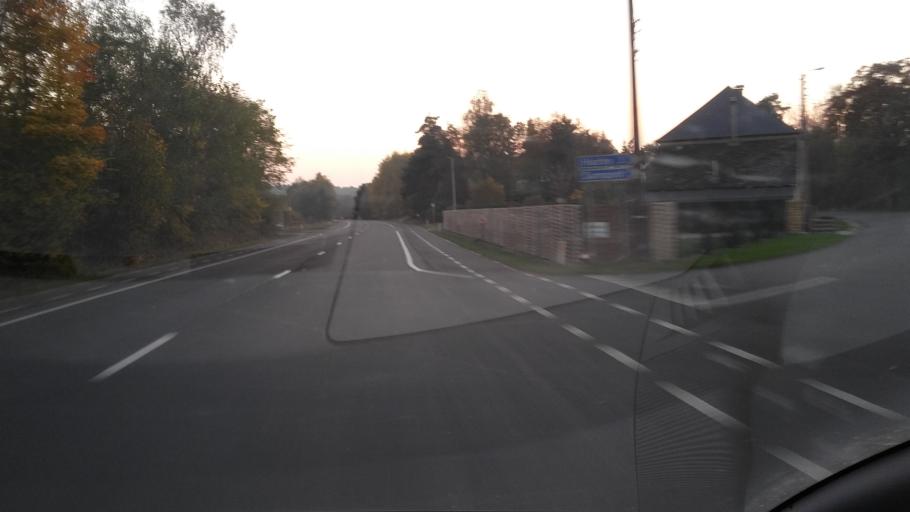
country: BE
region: Wallonia
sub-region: Province du Luxembourg
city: Saint-Leger
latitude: 49.6782
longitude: 5.7041
